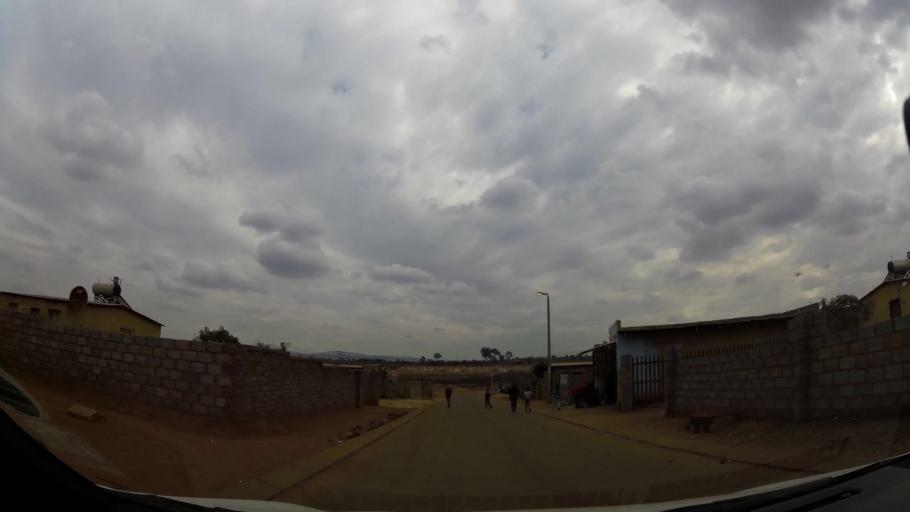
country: ZA
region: Gauteng
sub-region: Ekurhuleni Metropolitan Municipality
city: Germiston
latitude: -26.3750
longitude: 28.1185
